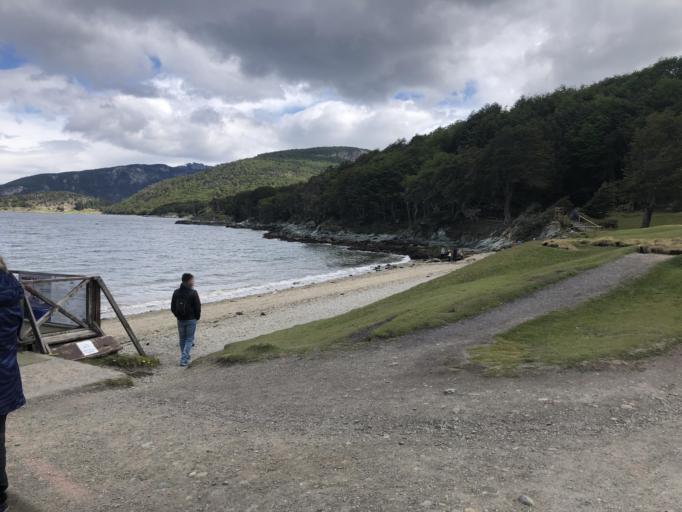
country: AR
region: Tierra del Fuego
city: Ushuaia
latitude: -54.8467
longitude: -68.4809
